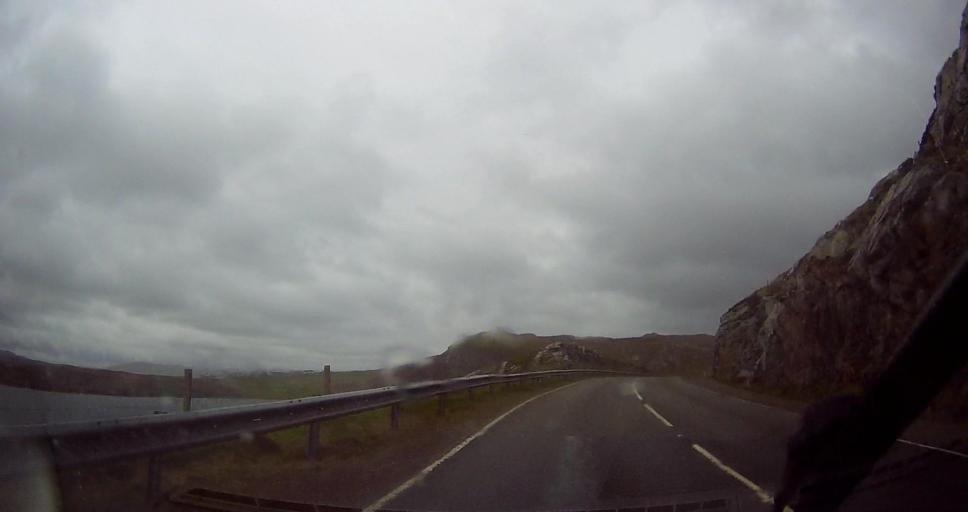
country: GB
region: Scotland
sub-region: Shetland Islands
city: Lerwick
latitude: 60.4016
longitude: -1.3835
